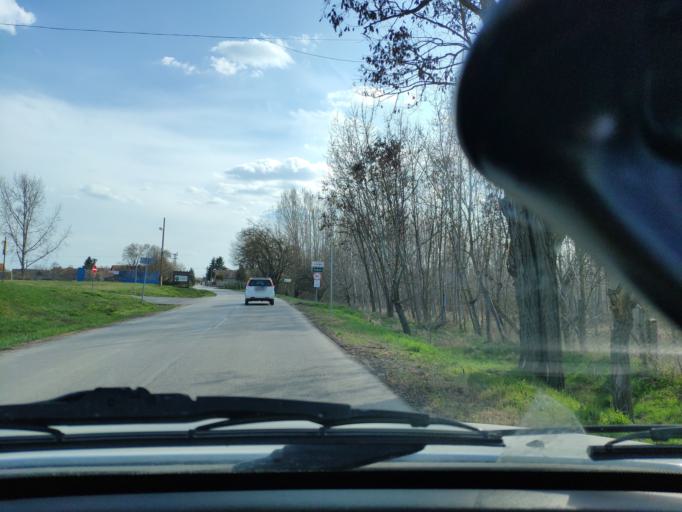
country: HU
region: Fejer
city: Adony
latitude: 47.1202
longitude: 18.8964
